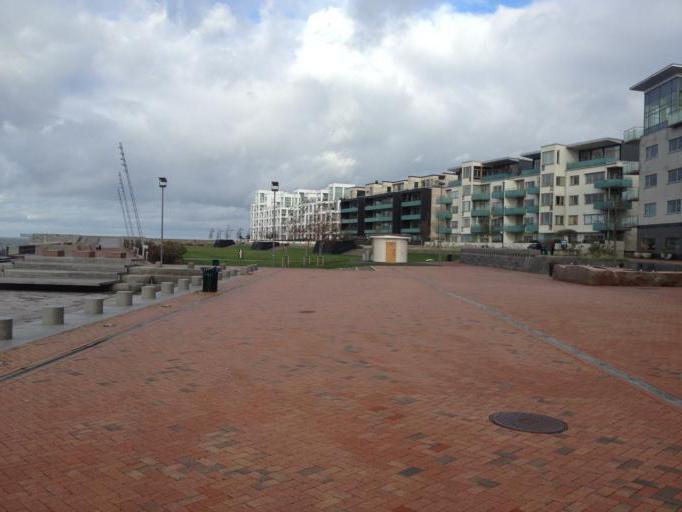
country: SE
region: Skane
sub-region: Malmo
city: Malmoe
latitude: 55.6125
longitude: 12.9722
